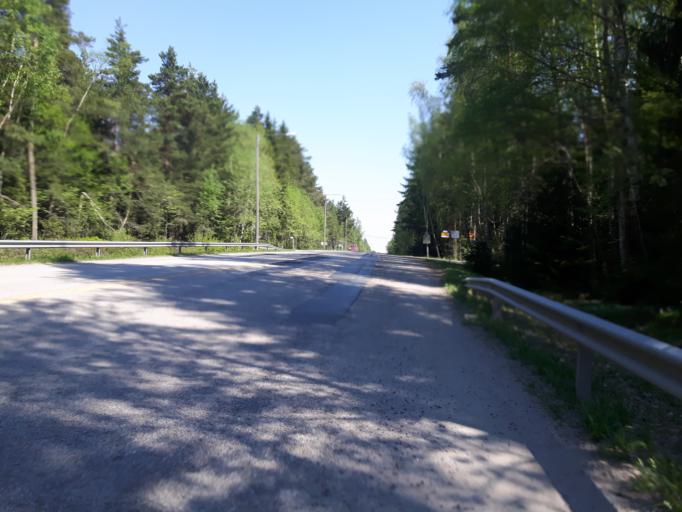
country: FI
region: Uusimaa
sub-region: Helsinki
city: Nickby
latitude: 60.2982
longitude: 25.3576
